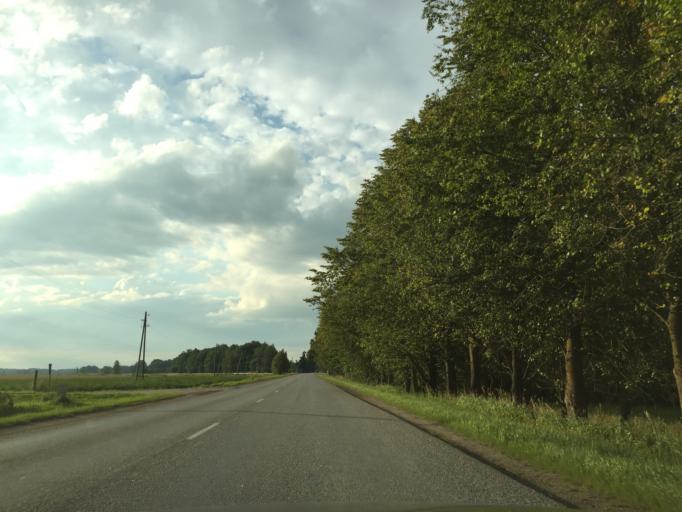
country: LV
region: Dobeles Rajons
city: Dobele
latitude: 56.7616
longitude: 23.3905
